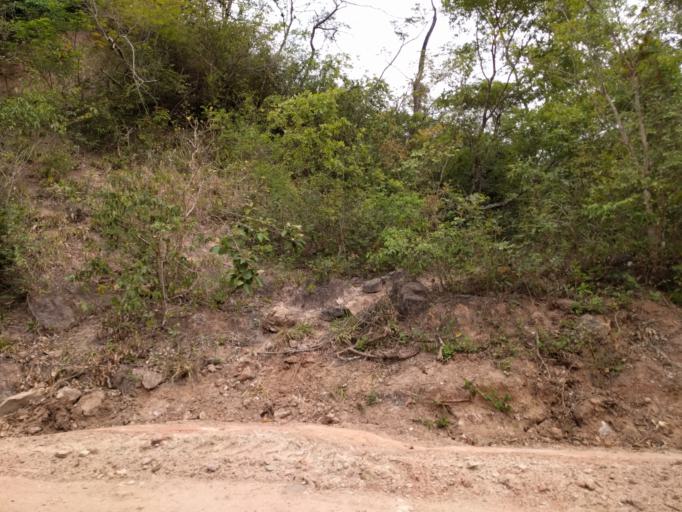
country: BO
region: Santa Cruz
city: Santiago del Torno
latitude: -17.9093
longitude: -63.4380
